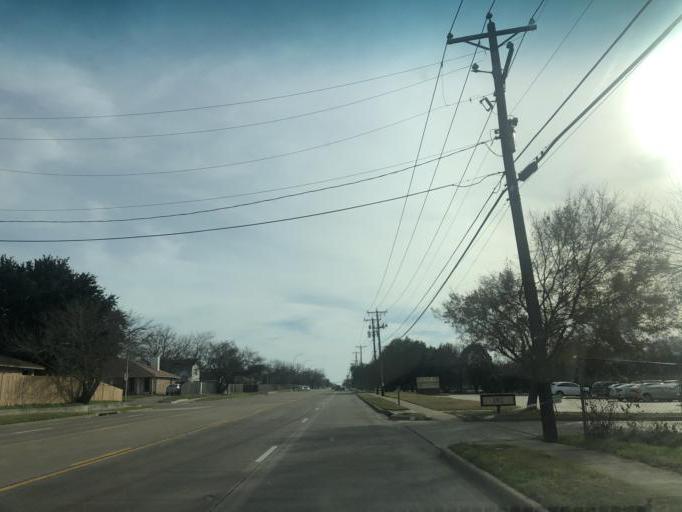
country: US
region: Texas
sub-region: Tarrant County
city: Dalworthington Gardens
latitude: 32.7051
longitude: -97.1493
